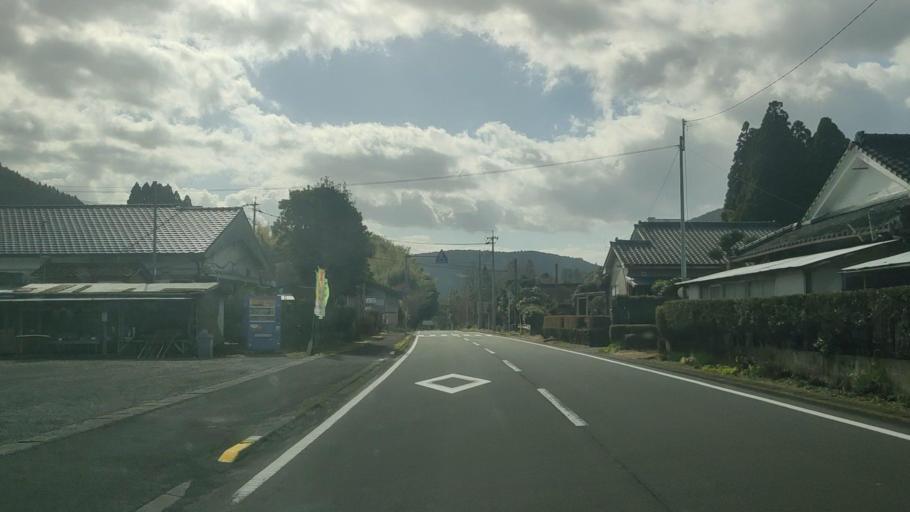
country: JP
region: Kagoshima
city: Okuchi-shinohara
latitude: 31.9887
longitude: 130.7443
